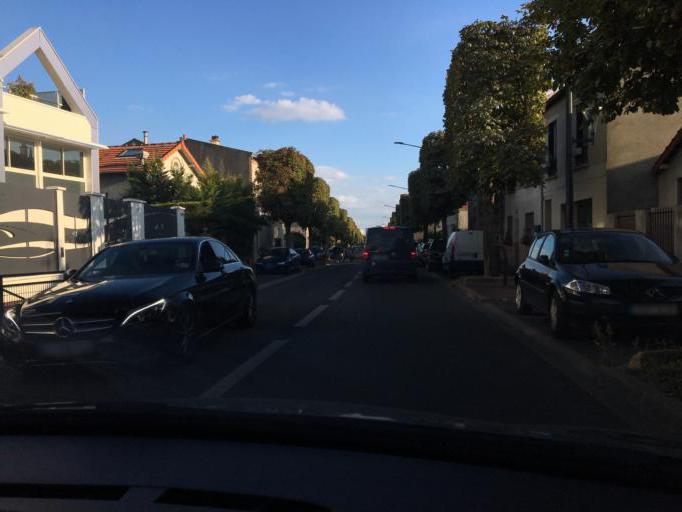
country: FR
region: Ile-de-France
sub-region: Departement du Val-de-Marne
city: Fontenay-sous-Bois
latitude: 48.8564
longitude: 2.4675
